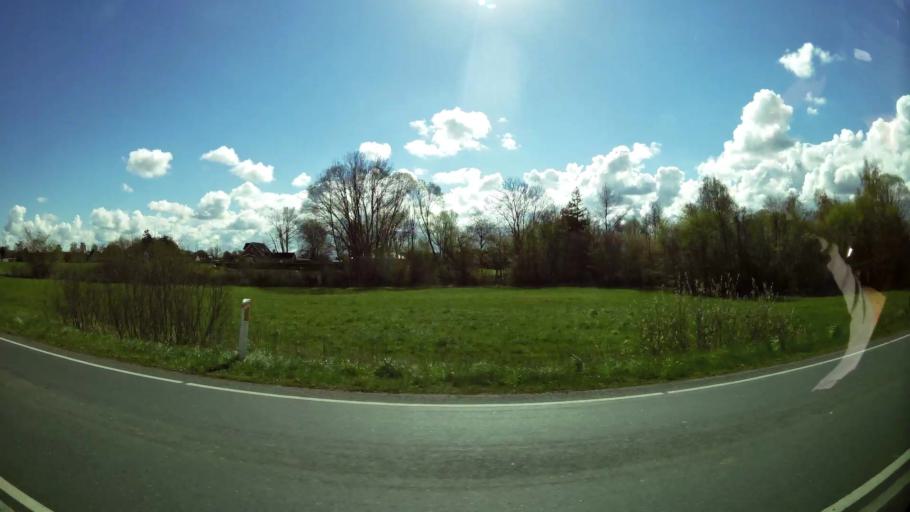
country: DK
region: South Denmark
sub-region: Middelfart Kommune
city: Brenderup
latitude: 55.4849
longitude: 9.9746
